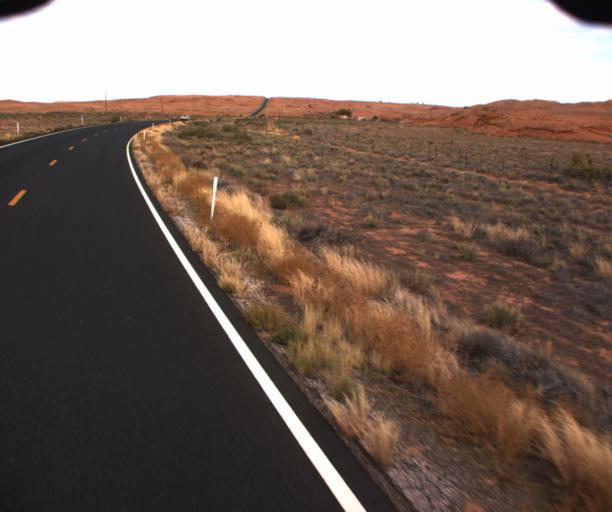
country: US
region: Arizona
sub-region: Apache County
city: Many Farms
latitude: 36.7745
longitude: -109.6613
